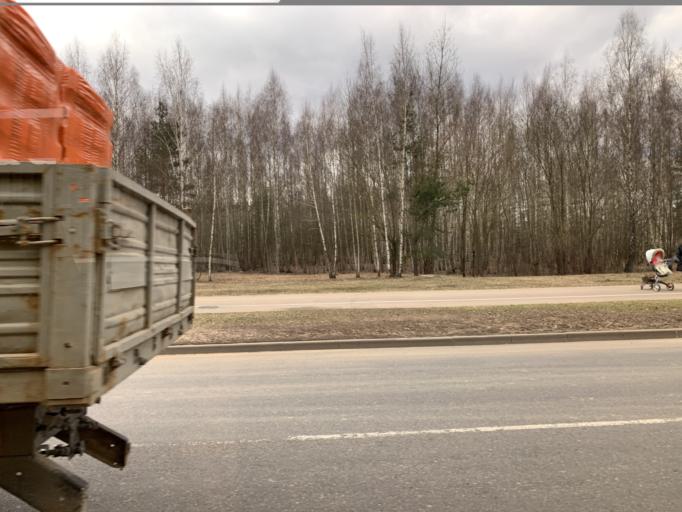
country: BY
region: Minsk
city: Lyeskawka
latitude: 53.9299
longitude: 27.6944
